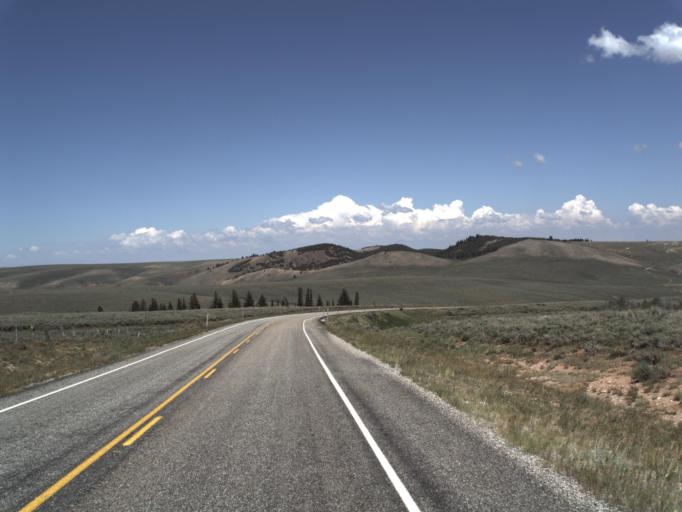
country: US
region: Utah
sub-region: Rich County
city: Randolph
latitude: 41.4787
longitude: -111.4325
